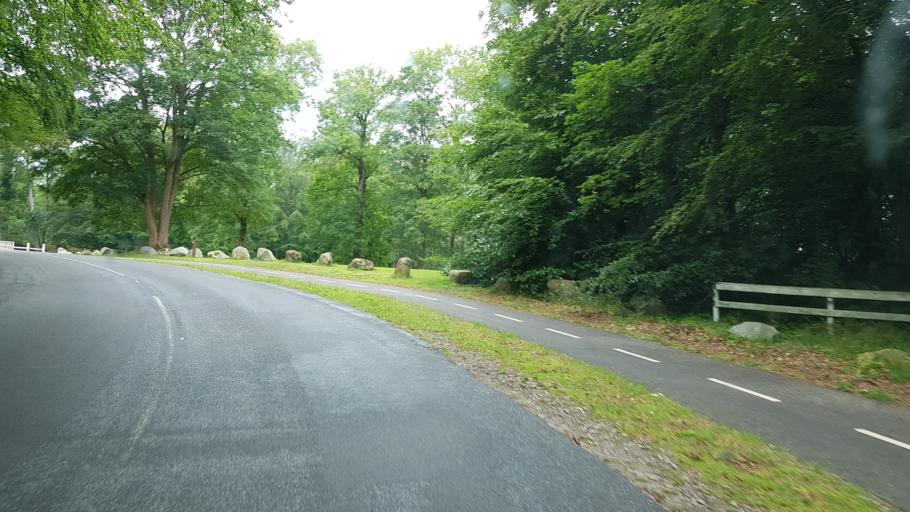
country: DK
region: South Denmark
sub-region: Varde Kommune
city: Olgod
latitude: 55.7054
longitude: 8.6466
